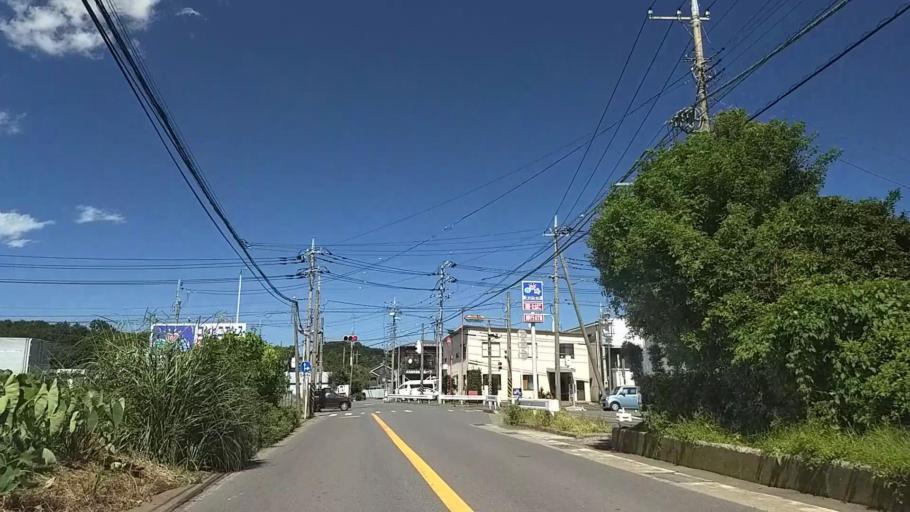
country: JP
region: Kanagawa
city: Zama
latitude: 35.5321
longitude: 139.3202
